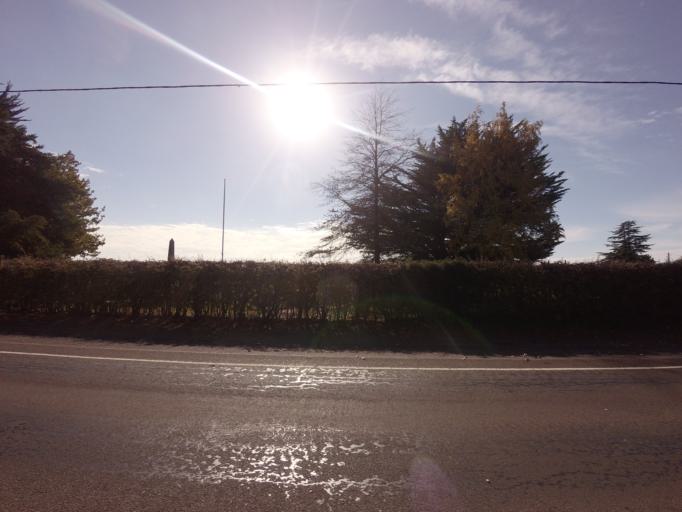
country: AU
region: Tasmania
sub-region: Meander Valley
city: Westbury
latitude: -41.5261
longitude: 146.8926
